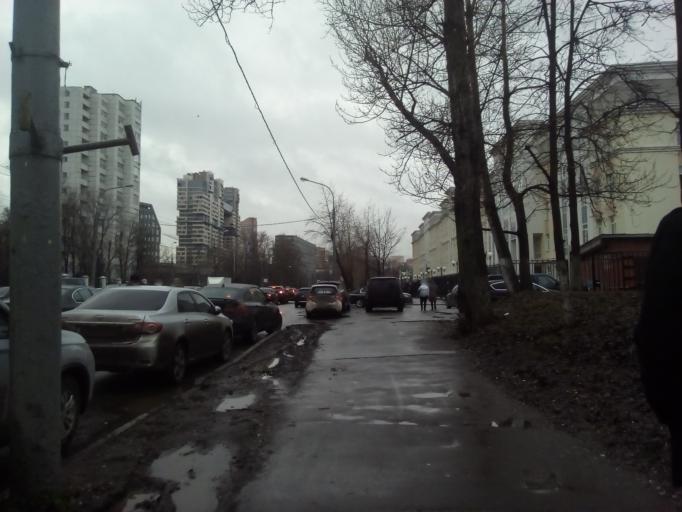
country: RU
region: Moskovskaya
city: Semenovskoye
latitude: 55.6866
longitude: 37.5551
